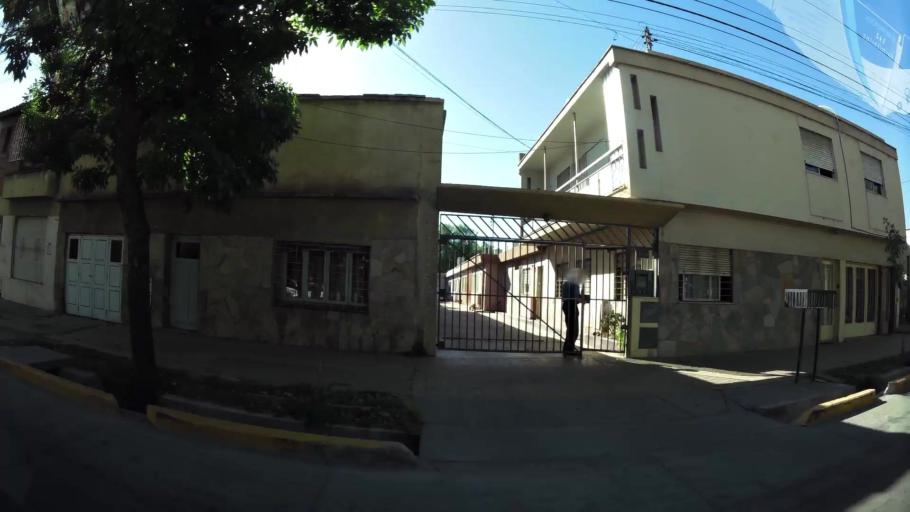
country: AR
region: Mendoza
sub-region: Departamento de Godoy Cruz
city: Godoy Cruz
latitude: -32.9216
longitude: -68.8425
